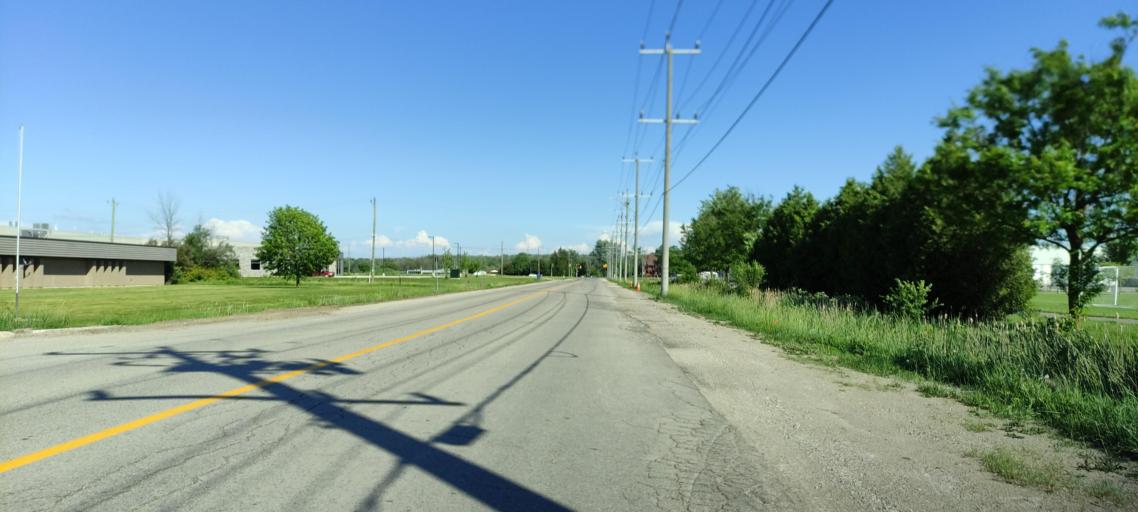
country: CA
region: Ontario
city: Stratford
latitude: 43.3497
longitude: -81.0067
